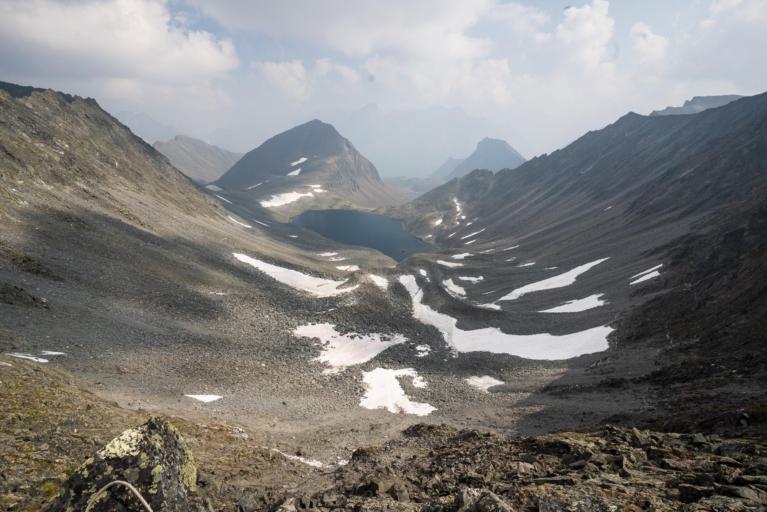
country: RU
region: Transbaikal Territory
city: Chara
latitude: 56.8332
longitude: 117.1762
